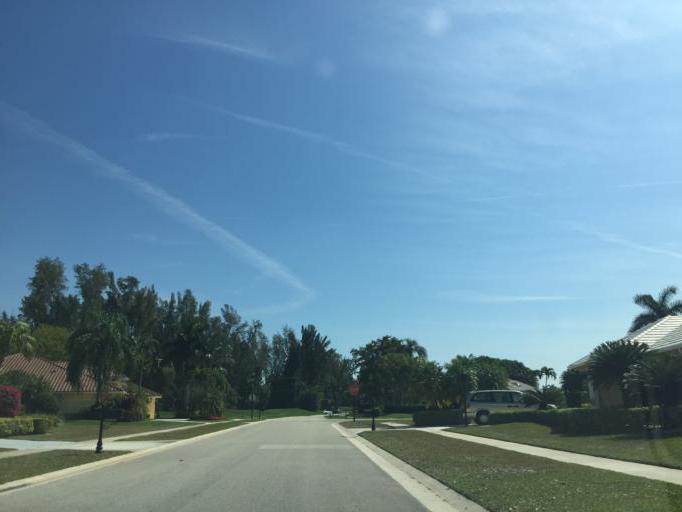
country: US
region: Florida
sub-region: Palm Beach County
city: Villages of Oriole
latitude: 26.4156
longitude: -80.2156
